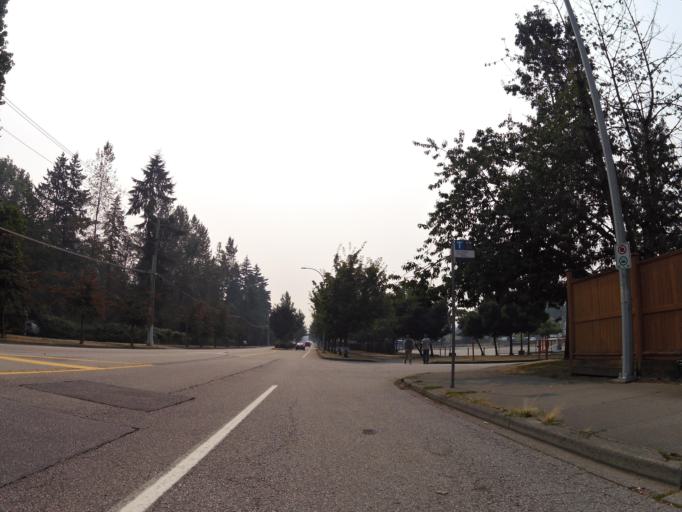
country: CA
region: British Columbia
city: Surrey
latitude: 49.1290
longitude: -122.8567
